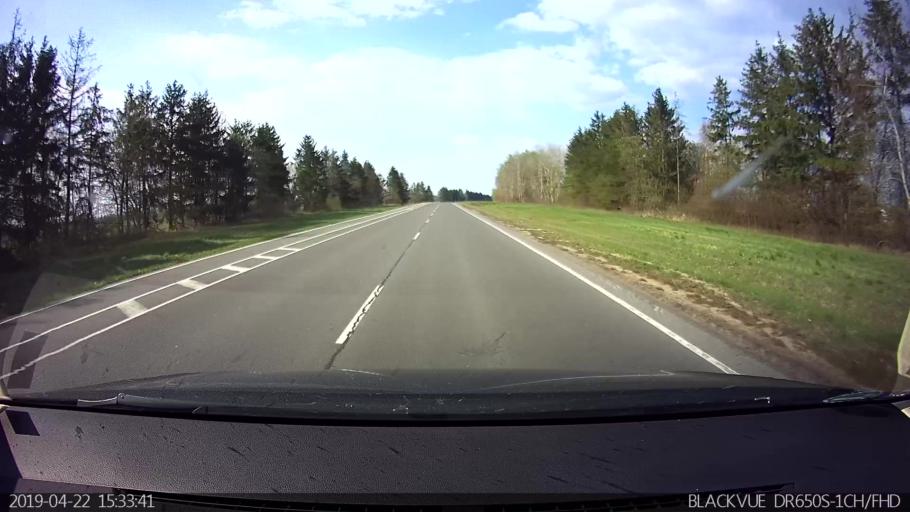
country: BY
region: Brest
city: Vysokaye
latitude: 52.4208
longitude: 23.3786
